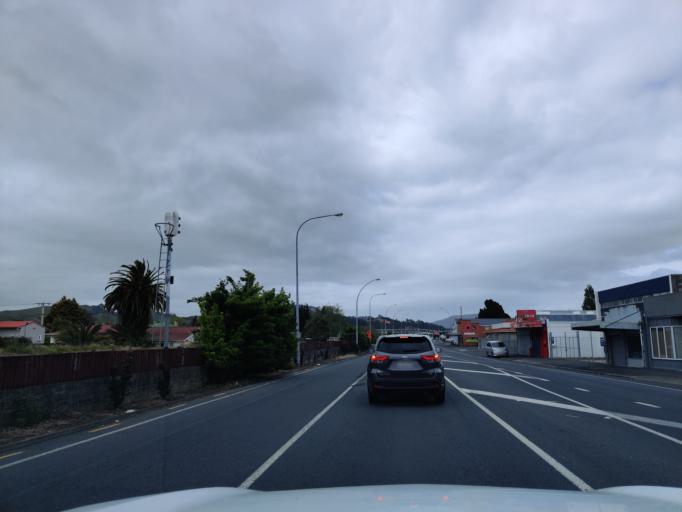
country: NZ
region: Waikato
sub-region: Waikato District
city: Ngaruawahia
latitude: -37.5542
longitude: 175.1591
